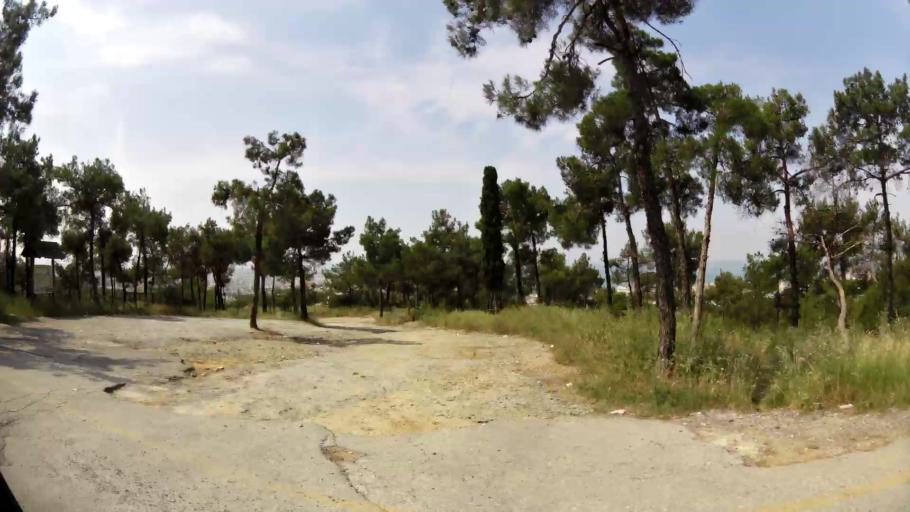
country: GR
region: Central Macedonia
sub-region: Nomos Thessalonikis
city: Agios Pavlos
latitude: 40.6347
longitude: 22.9692
